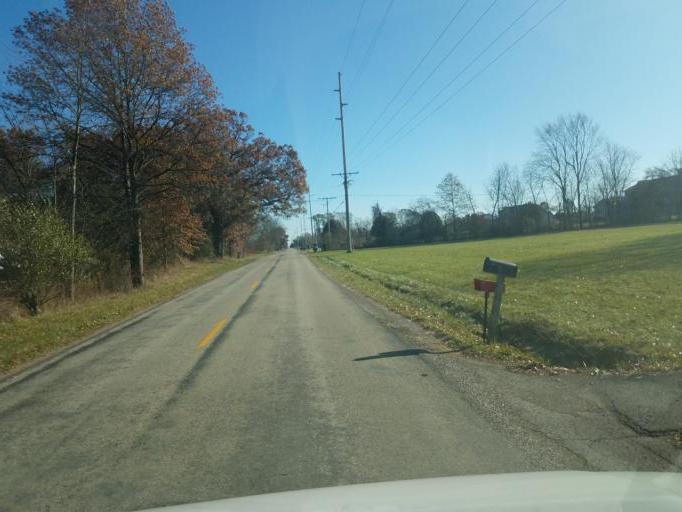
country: US
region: Ohio
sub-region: Ashland County
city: Ashland
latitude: 40.8290
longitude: -82.3441
